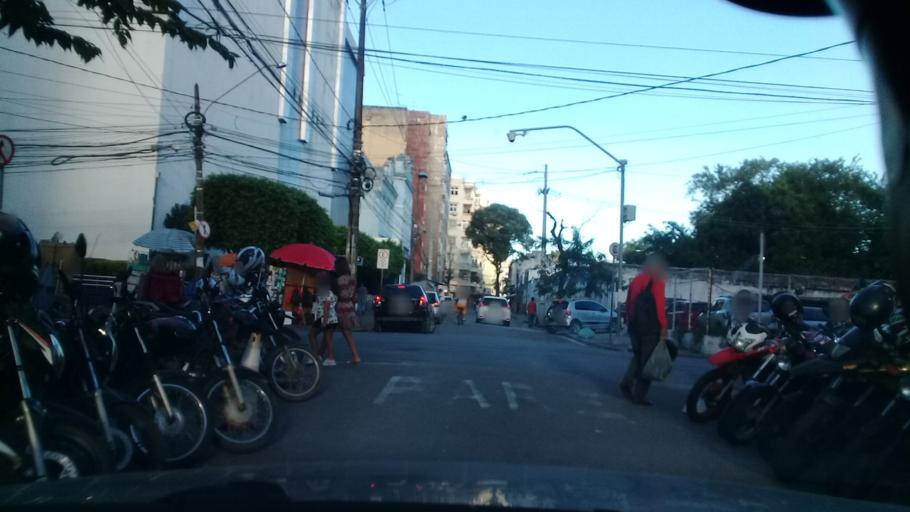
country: BR
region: Pernambuco
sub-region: Recife
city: Recife
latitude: -8.0598
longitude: -34.8882
